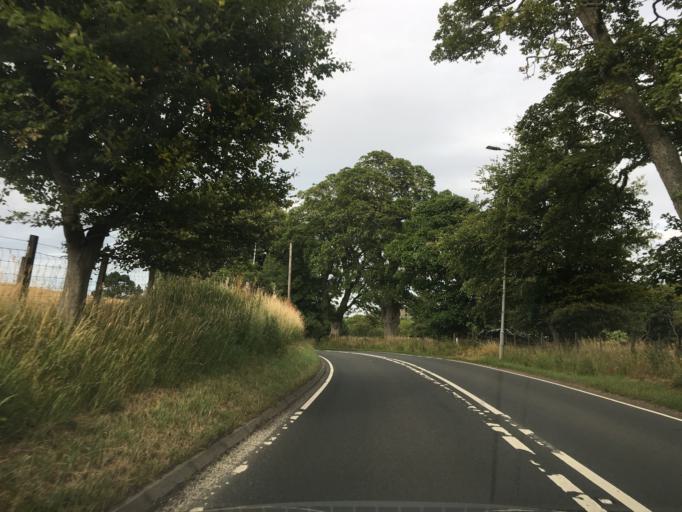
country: GB
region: Scotland
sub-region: South Lanarkshire
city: Biggar
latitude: 55.5879
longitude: -3.5532
